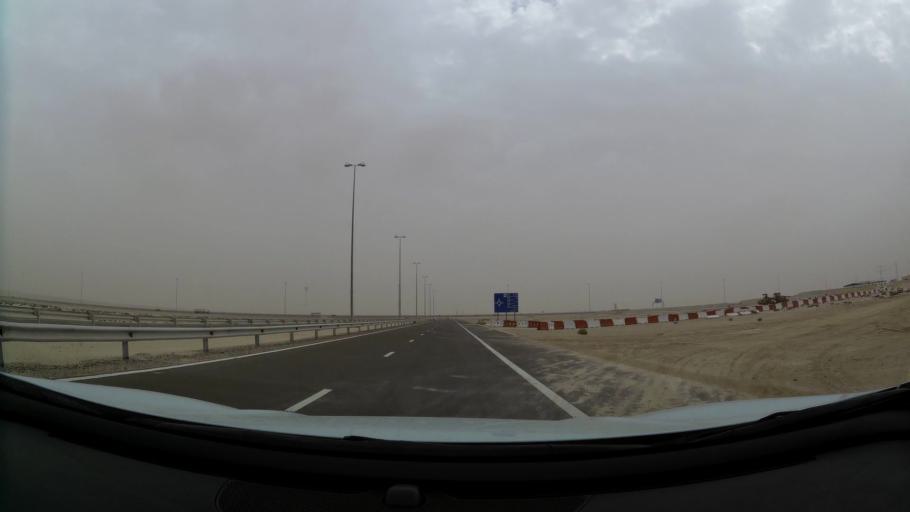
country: AE
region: Abu Dhabi
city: Abu Dhabi
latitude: 24.4320
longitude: 54.7614
